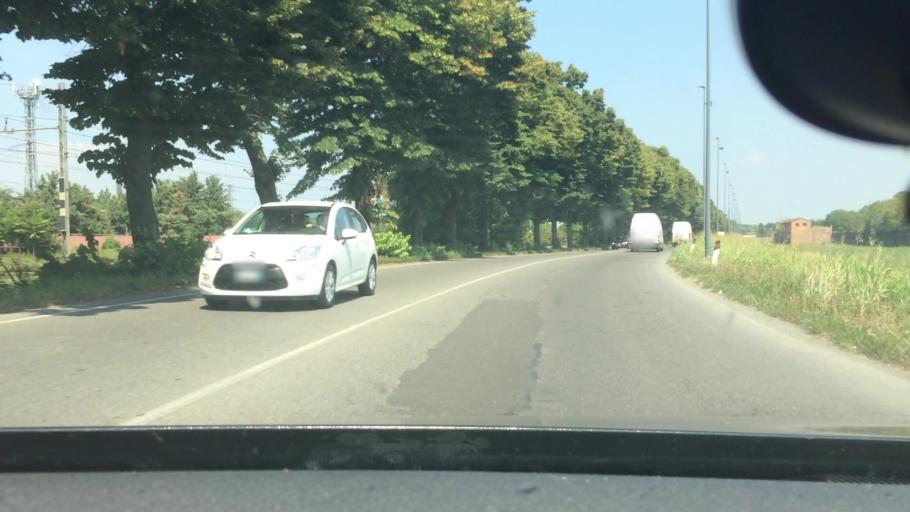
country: IT
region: Lombardy
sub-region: Provincia di Lodi
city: San Rocco al Porto
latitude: 45.0588
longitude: 9.6802
